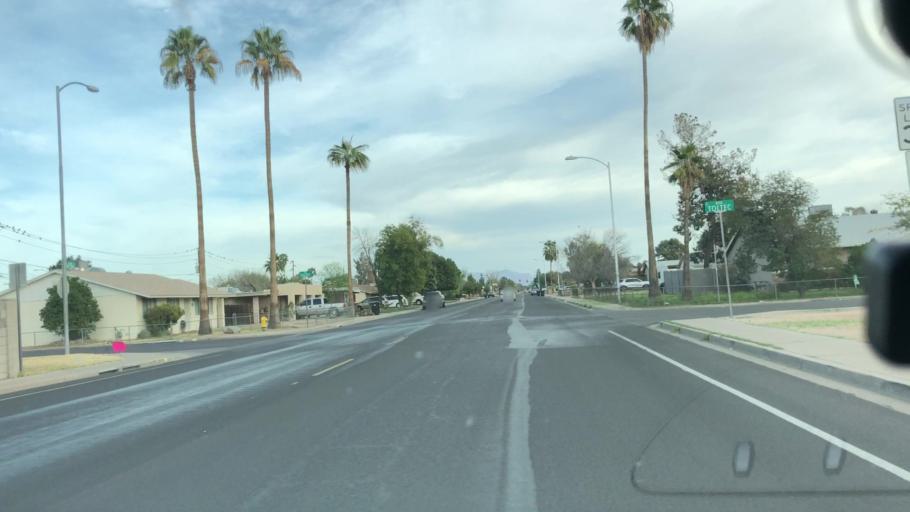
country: US
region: Arizona
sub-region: Maricopa County
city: Mesa
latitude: 33.4008
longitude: -111.7924
